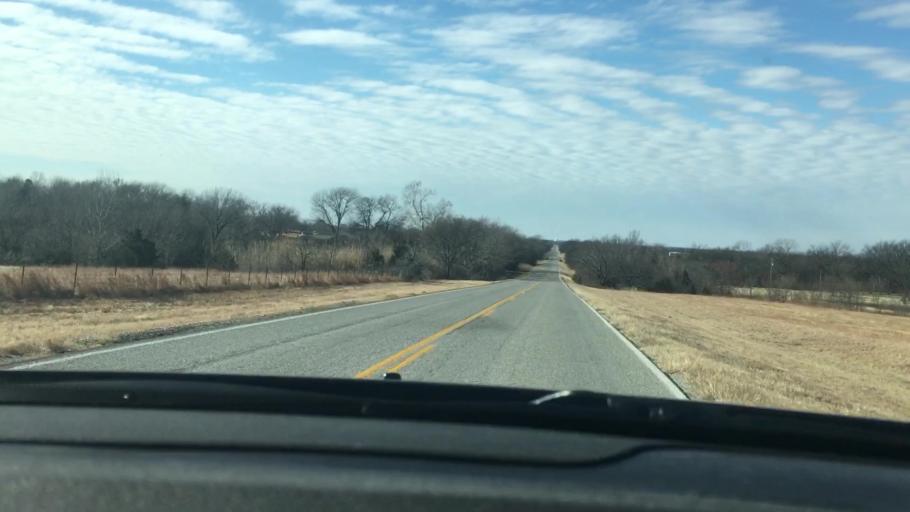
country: US
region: Oklahoma
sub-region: Garvin County
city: Wynnewood
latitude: 34.6515
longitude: -97.1107
